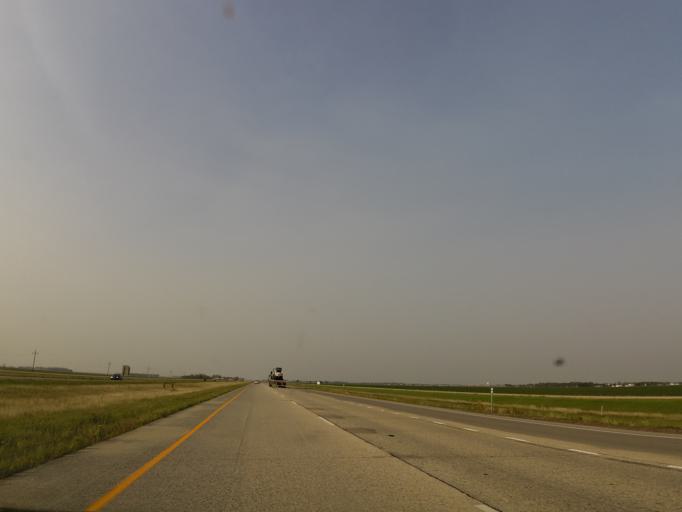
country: US
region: North Dakota
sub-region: Cass County
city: Horace
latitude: 46.7486
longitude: -96.8396
